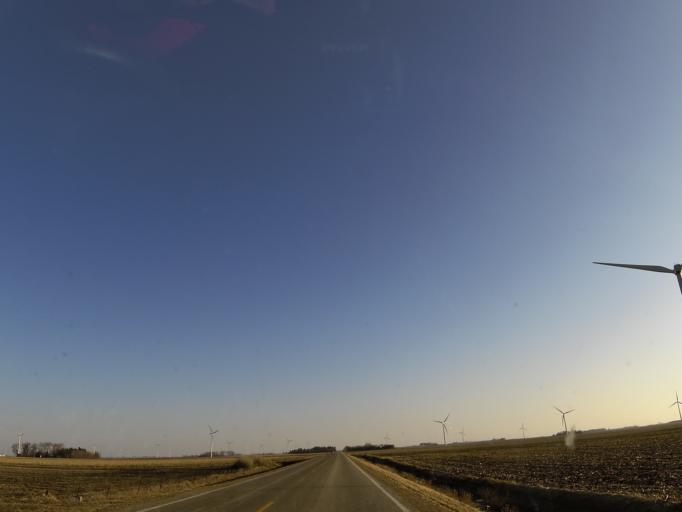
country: US
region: Iowa
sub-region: Worth County
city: Northwood
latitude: 43.4240
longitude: -93.1244
